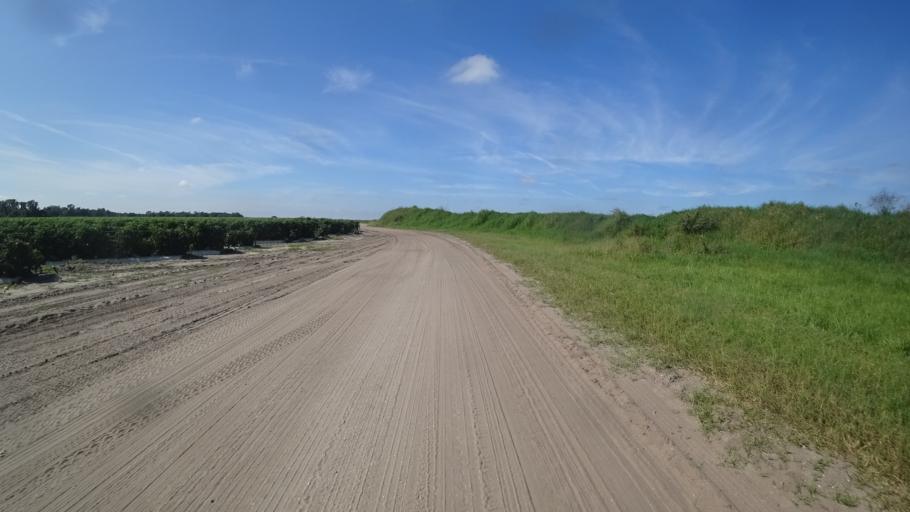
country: US
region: Florida
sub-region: DeSoto County
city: Arcadia
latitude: 27.2944
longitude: -82.0447
